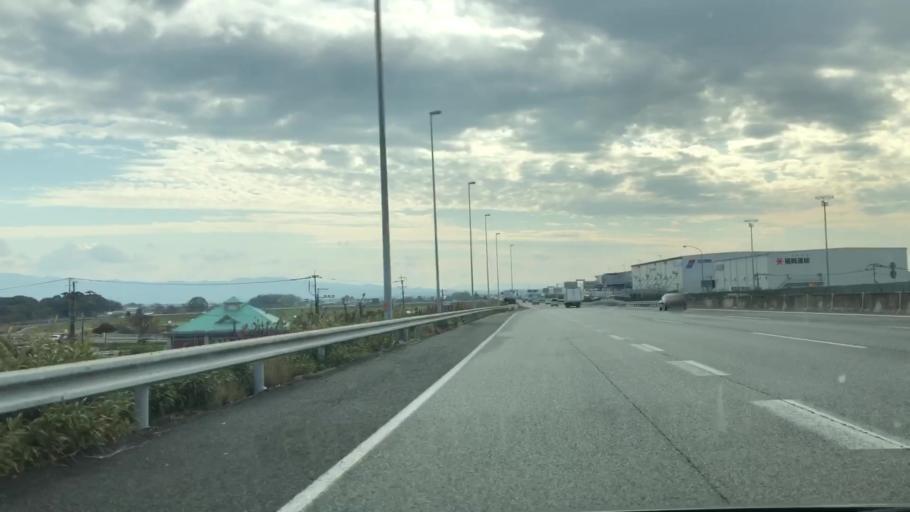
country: JP
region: Saga Prefecture
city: Tosu
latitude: 33.3934
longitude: 130.5385
